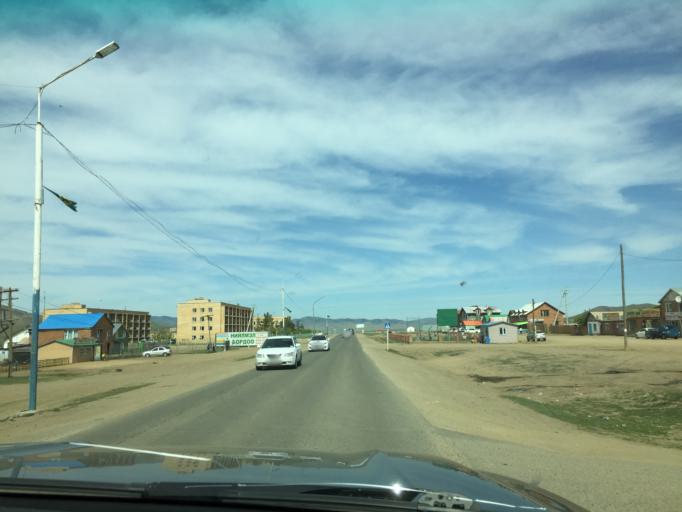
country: MN
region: Central Aimak
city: Ihsueuej
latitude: 48.2246
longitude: 106.2929
